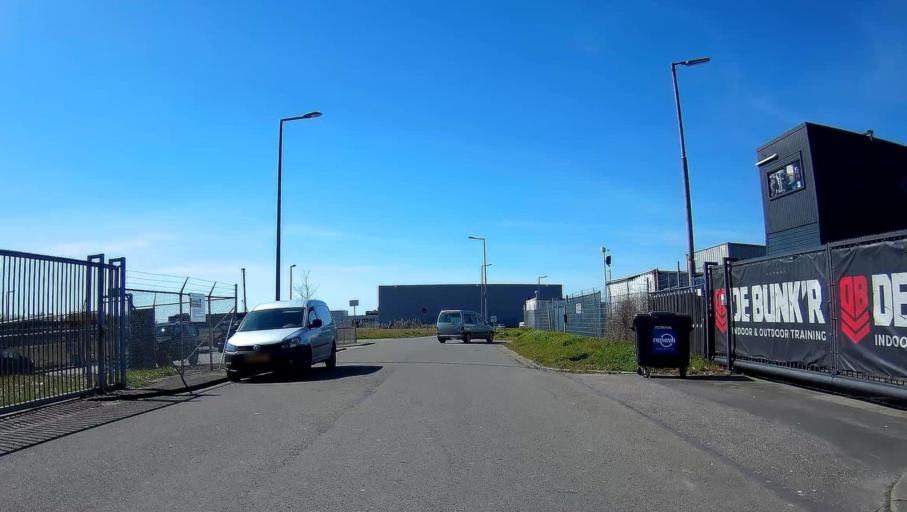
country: NL
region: South Holland
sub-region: Gemeente Rotterdam
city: Rotterdam
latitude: 51.9550
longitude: 4.4509
